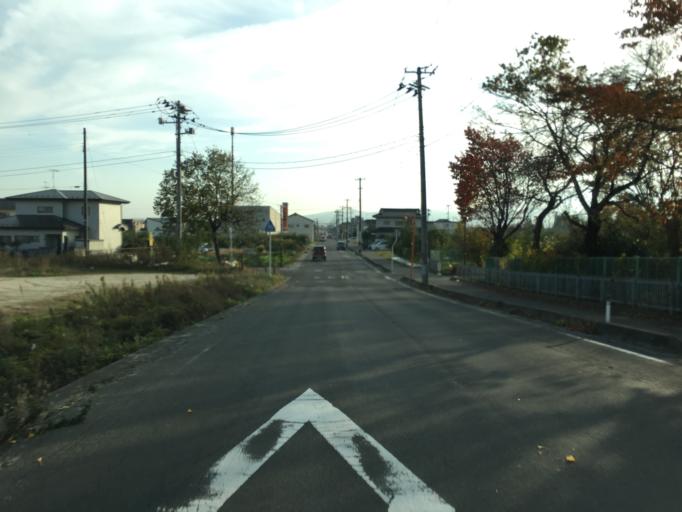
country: JP
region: Fukushima
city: Fukushima-shi
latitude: 37.7804
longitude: 140.4260
